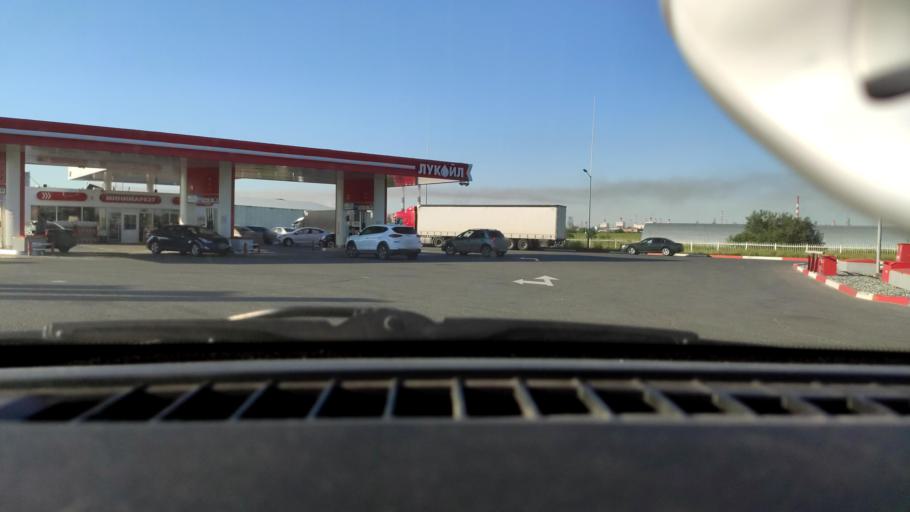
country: RU
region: Perm
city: Kondratovo
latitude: 57.9420
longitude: 56.1408
